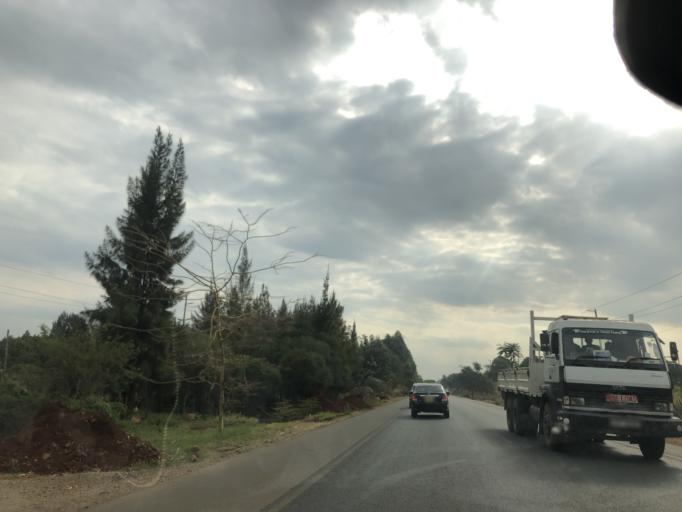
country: KE
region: Kiambu
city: Kiambu
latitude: -1.2152
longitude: 36.8604
